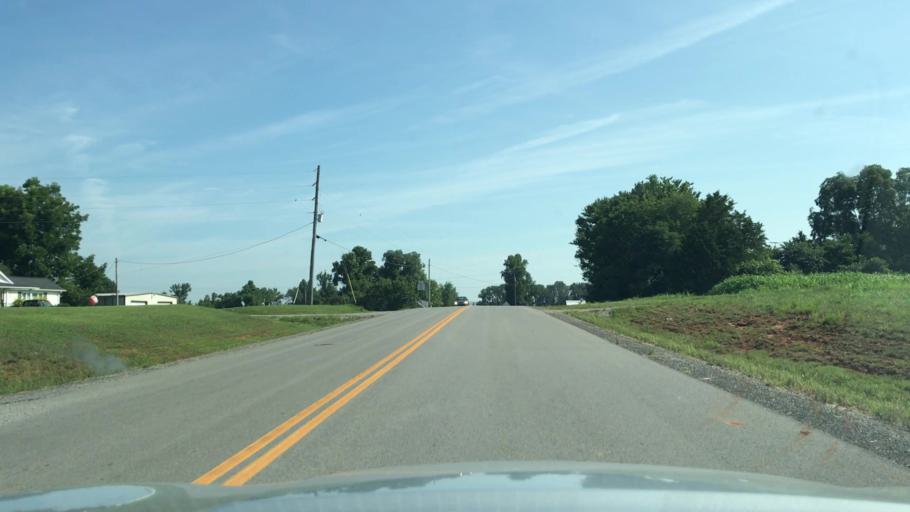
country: US
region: Tennessee
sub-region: Pickett County
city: Byrdstown
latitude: 36.6222
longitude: -85.0854
